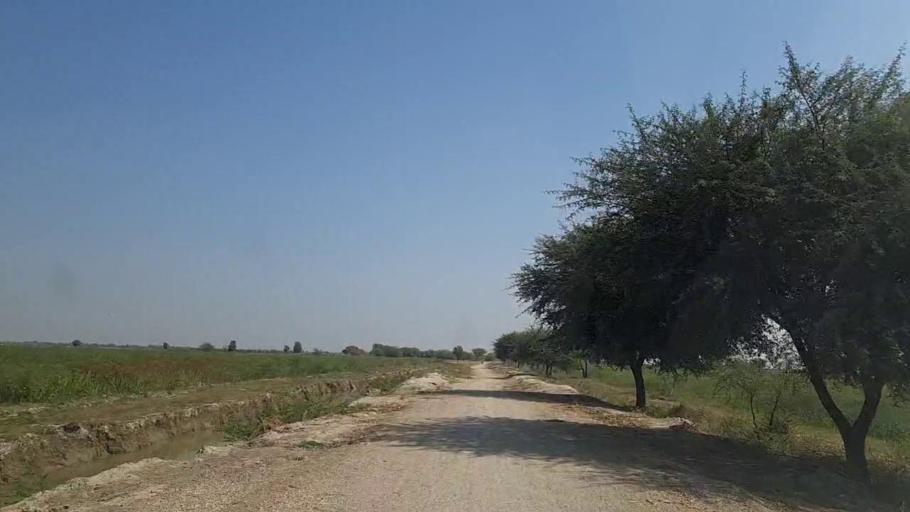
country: PK
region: Sindh
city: Naukot
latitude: 24.8794
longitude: 69.3868
